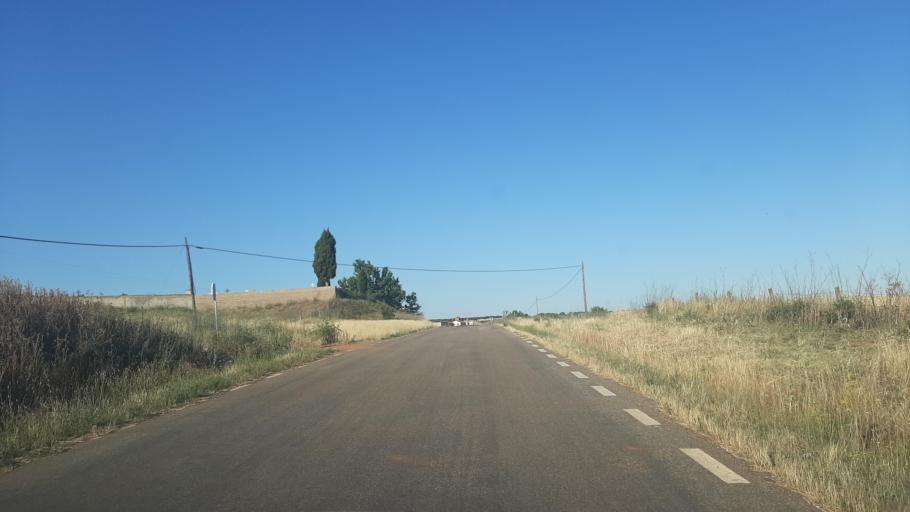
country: ES
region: Castille and Leon
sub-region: Provincia de Salamanca
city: Cabrillas
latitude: 40.7046
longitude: -6.1809
